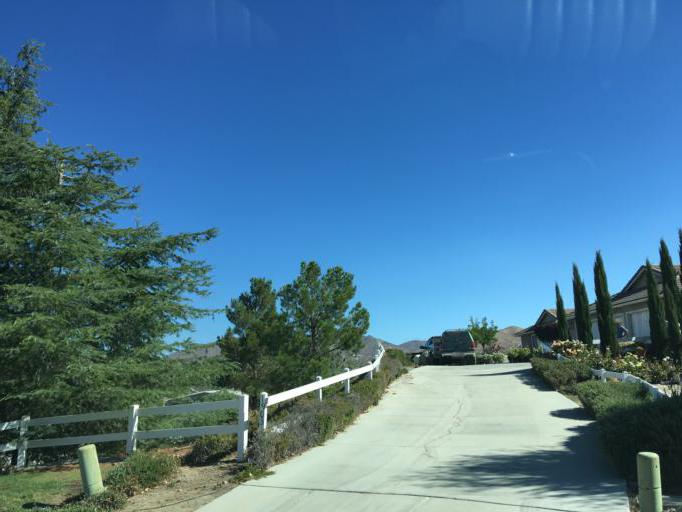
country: US
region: California
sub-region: Los Angeles County
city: Acton
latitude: 34.4728
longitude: -118.1572
